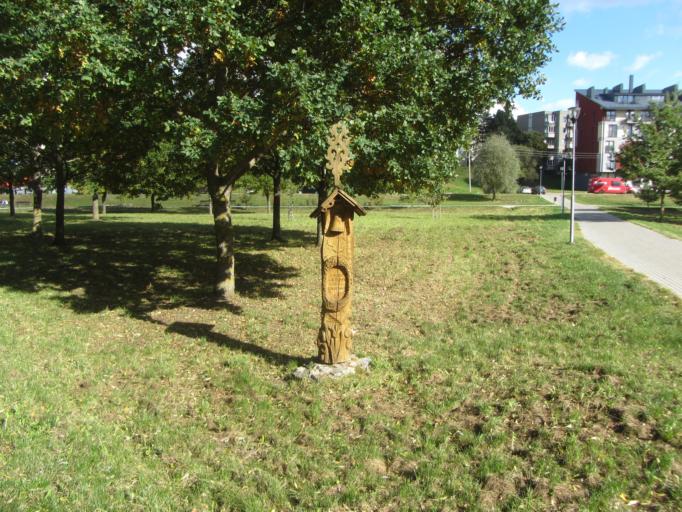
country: LT
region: Utenos apskritis
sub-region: Utena
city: Utena
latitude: 55.4953
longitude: 25.6116
